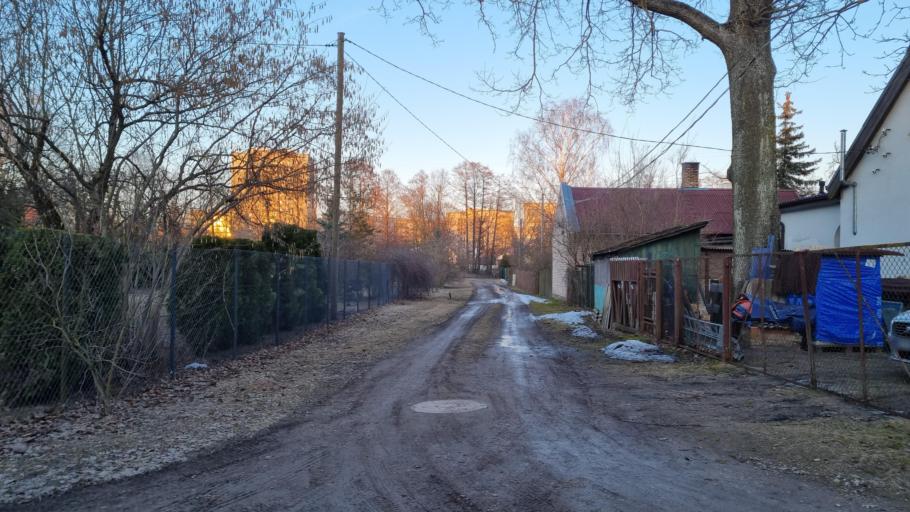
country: LV
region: Marupe
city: Marupe
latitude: 56.9467
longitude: 23.9961
